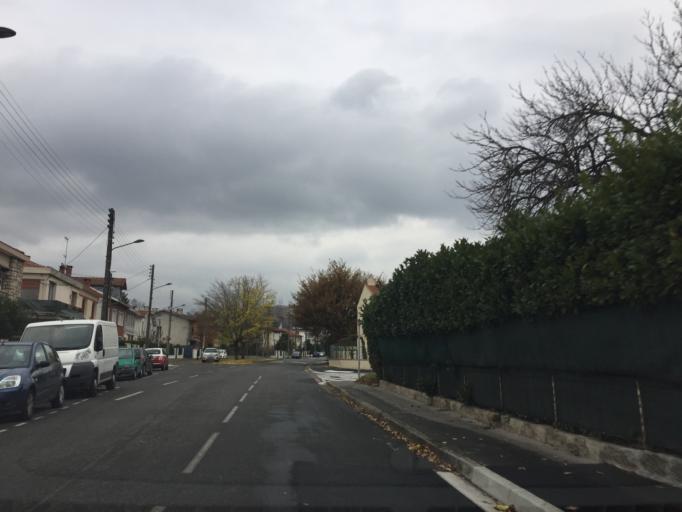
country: FR
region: Midi-Pyrenees
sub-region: Departement de la Haute-Garonne
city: Ramonville-Saint-Agne
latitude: 43.5701
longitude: 1.4617
